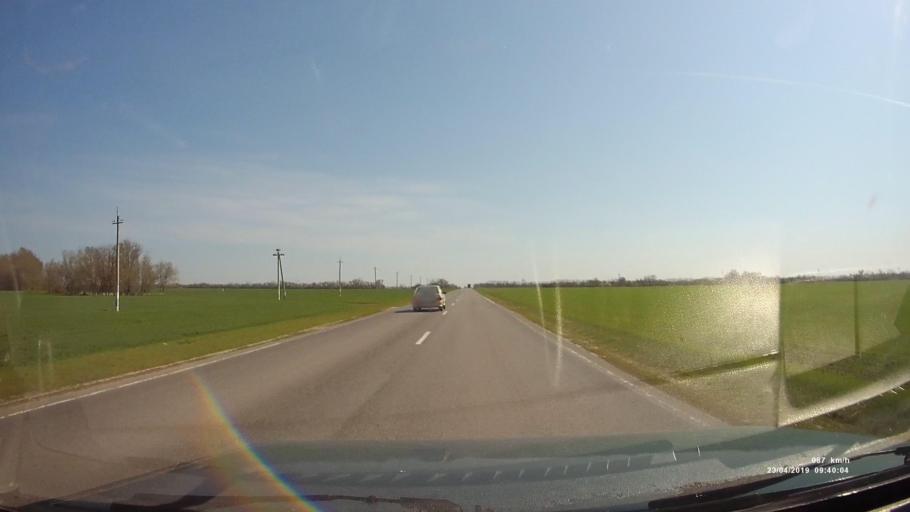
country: RU
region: Rostov
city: Gundorovskiy
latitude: 46.8570
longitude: 41.9373
